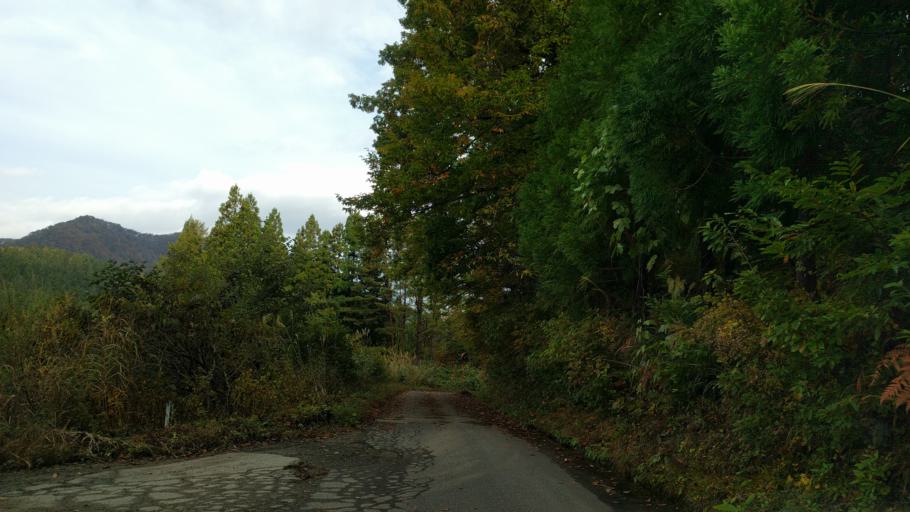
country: JP
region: Fukushima
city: Kitakata
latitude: 37.3904
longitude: 139.7035
